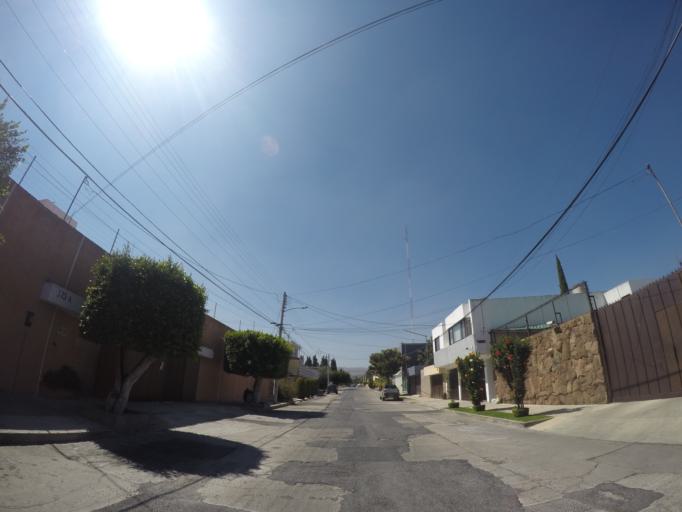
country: MX
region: San Luis Potosi
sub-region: San Luis Potosi
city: San Luis Potosi
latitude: 22.1460
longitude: -101.0115
